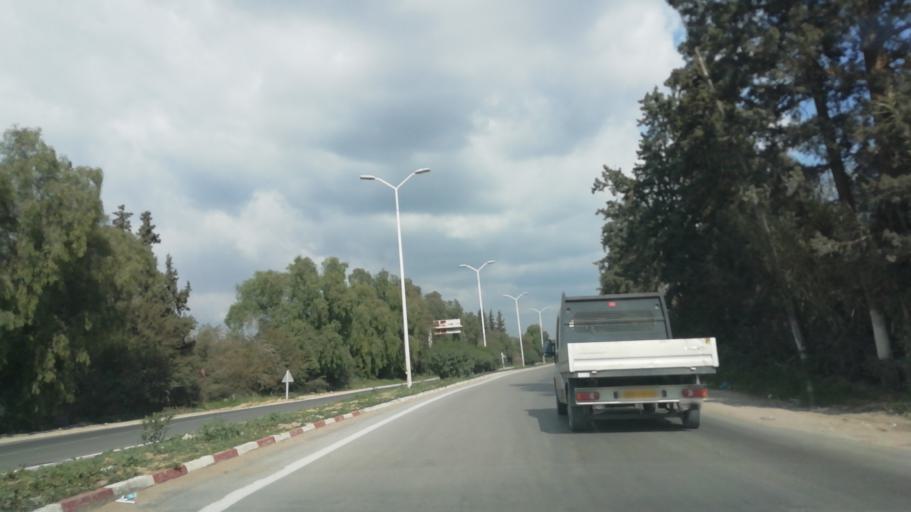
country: DZ
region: Mascara
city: Mascara
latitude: 35.5984
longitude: 0.0802
